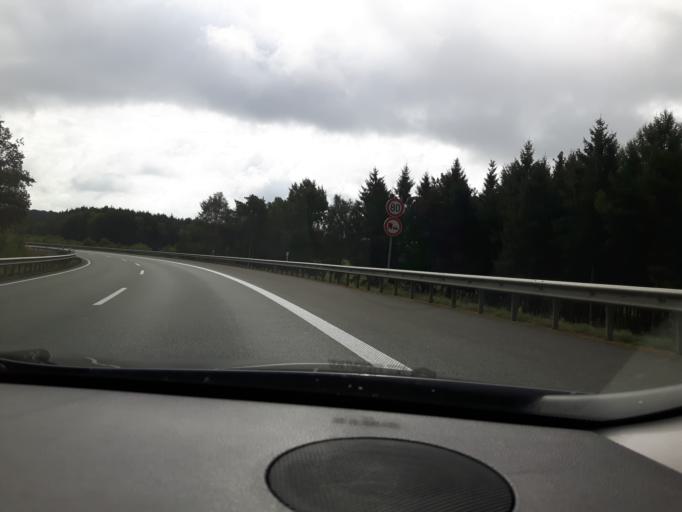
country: DE
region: Lower Saxony
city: Buchholz in der Nordheide
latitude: 53.3714
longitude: 9.8476
